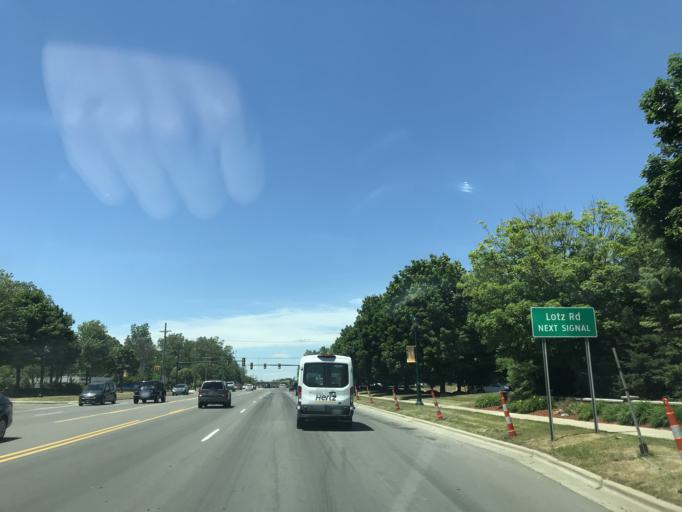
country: US
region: Michigan
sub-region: Wayne County
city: Westland
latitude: 42.3235
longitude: -83.4322
